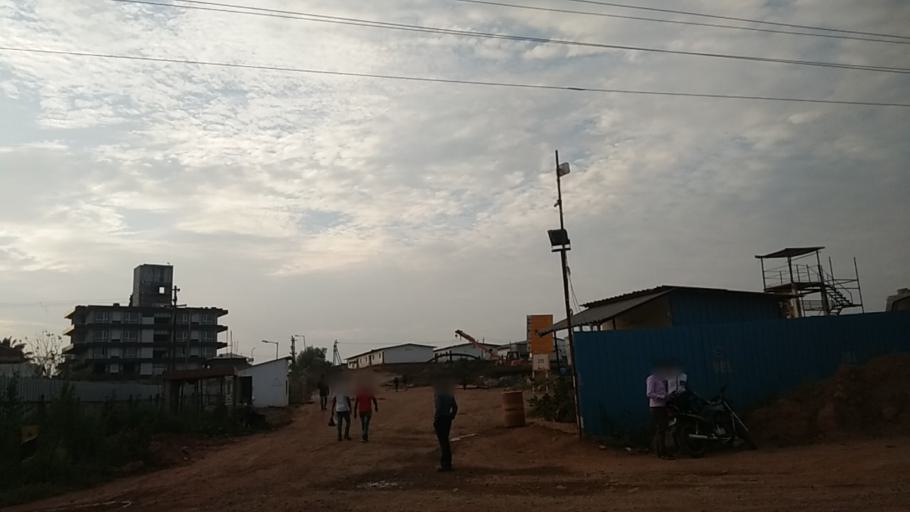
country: IN
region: Goa
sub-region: South Goa
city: Sancoale
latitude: 15.3666
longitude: 73.9262
